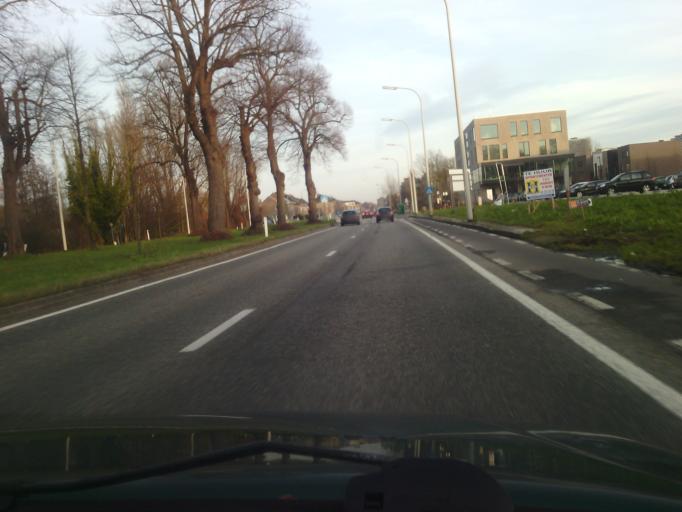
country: BE
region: Flanders
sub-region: Provincie Oost-Vlaanderen
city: Gent
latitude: 51.0551
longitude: 3.6882
